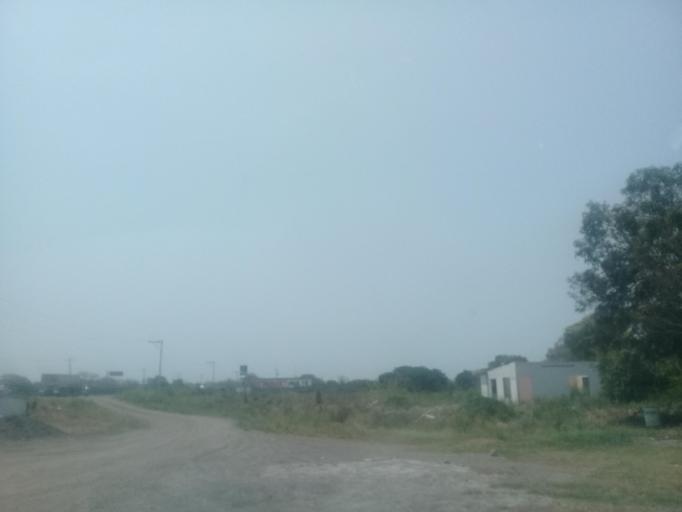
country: MX
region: Veracruz
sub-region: Veracruz
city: Hacienda Sotavento
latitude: 19.0953
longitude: -96.2091
